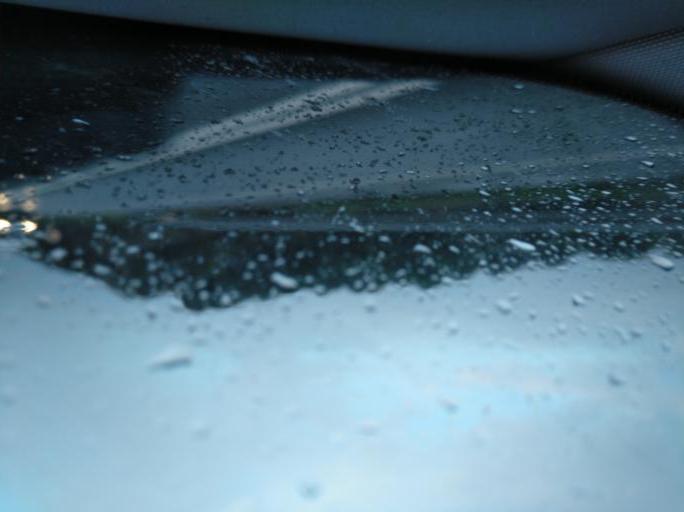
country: PT
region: Faro
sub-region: Castro Marim
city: Castro Marim
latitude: 37.2654
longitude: -7.4950
